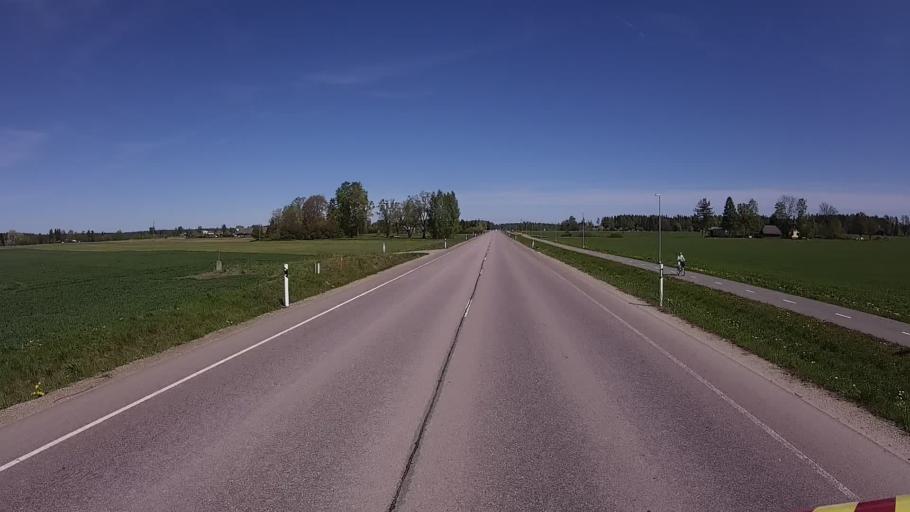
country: EE
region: Polvamaa
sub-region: Polva linn
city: Polva
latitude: 58.0776
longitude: 27.0890
